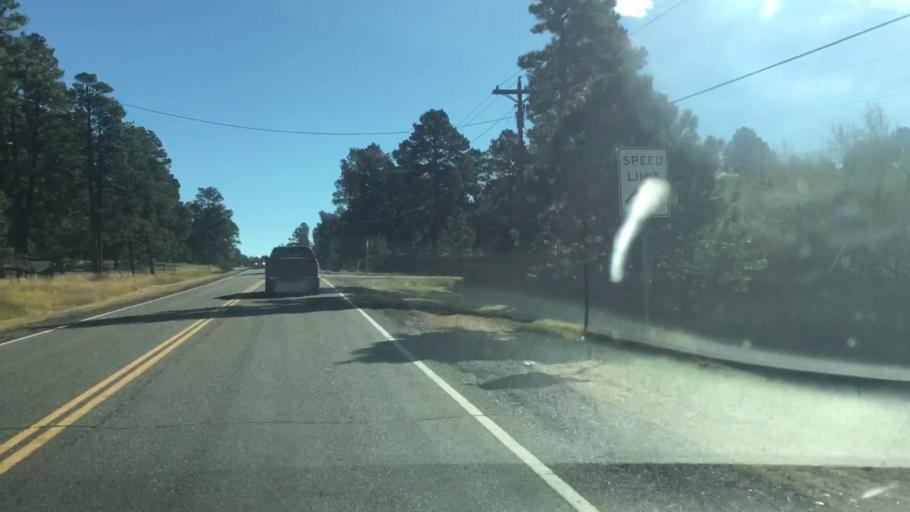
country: US
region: Colorado
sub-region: Elbert County
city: Elizabeth
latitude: 39.3614
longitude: -104.5856
